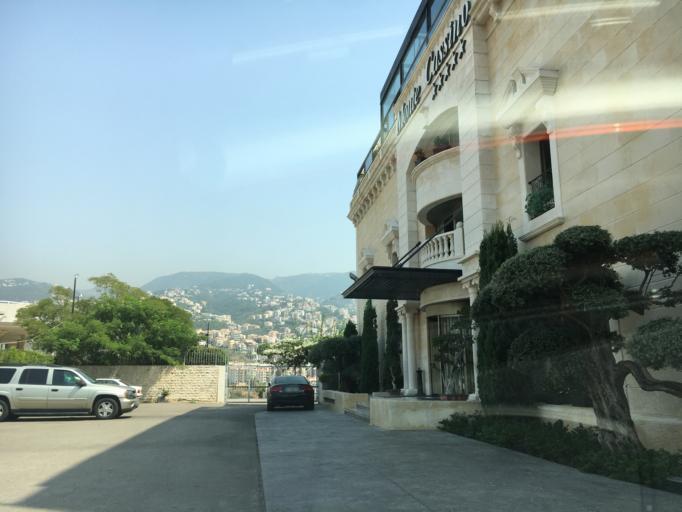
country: LB
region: Mont-Liban
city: Djounie
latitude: 34.0142
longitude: 35.6387
